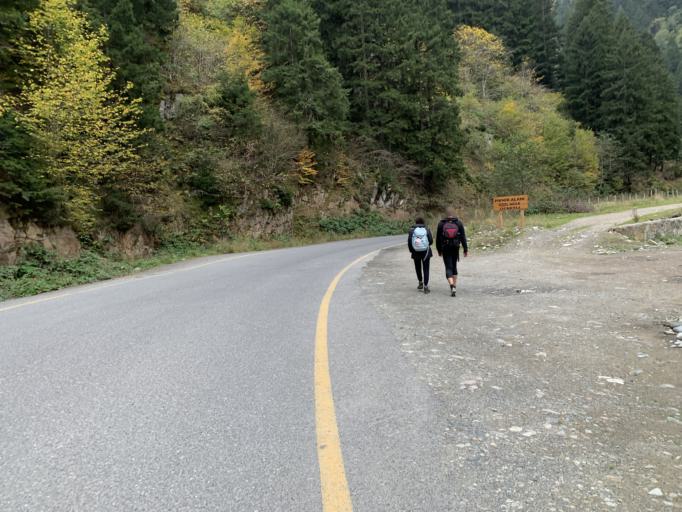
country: TR
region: Trabzon
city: Uzungol
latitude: 40.6025
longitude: 40.3176
